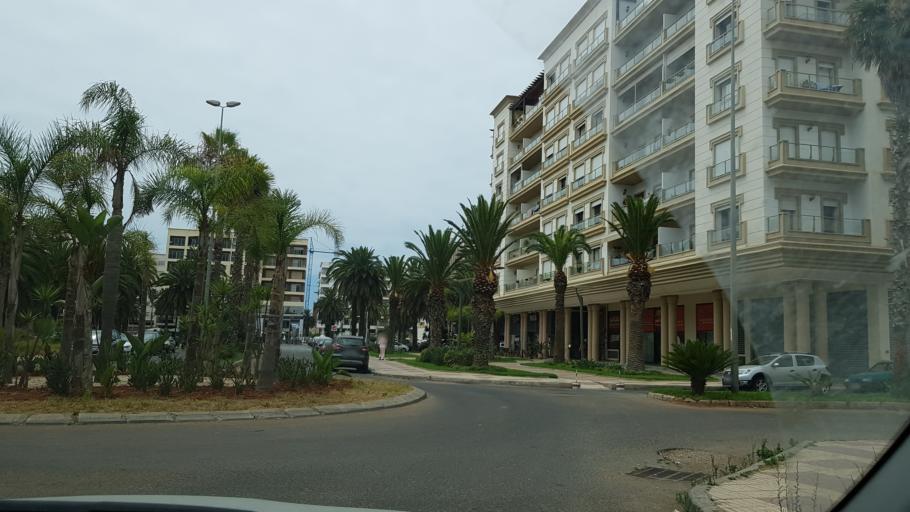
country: MA
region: Grand Casablanca
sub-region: Mohammedia
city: Mohammedia
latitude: 33.7043
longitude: -7.3972
